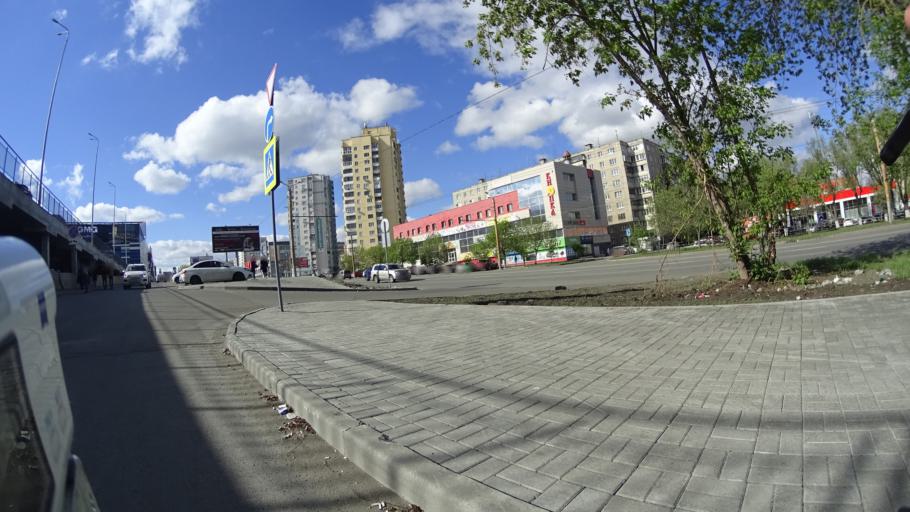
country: RU
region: Chelyabinsk
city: Roshchino
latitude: 55.1797
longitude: 61.2957
